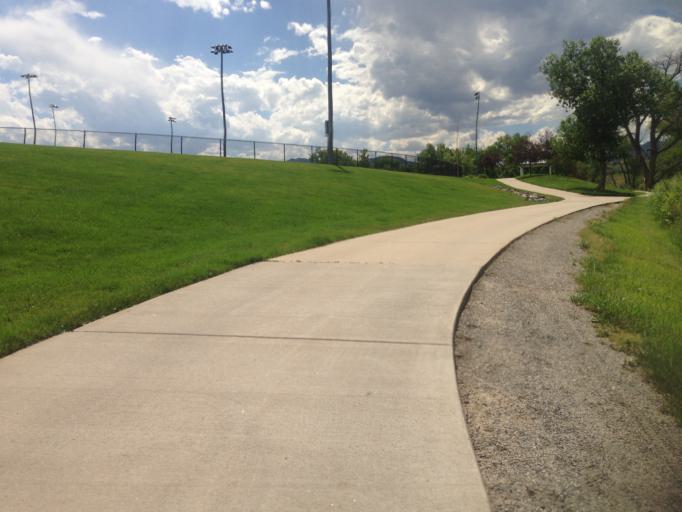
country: US
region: Colorado
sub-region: Boulder County
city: Superior
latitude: 39.9312
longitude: -105.1506
